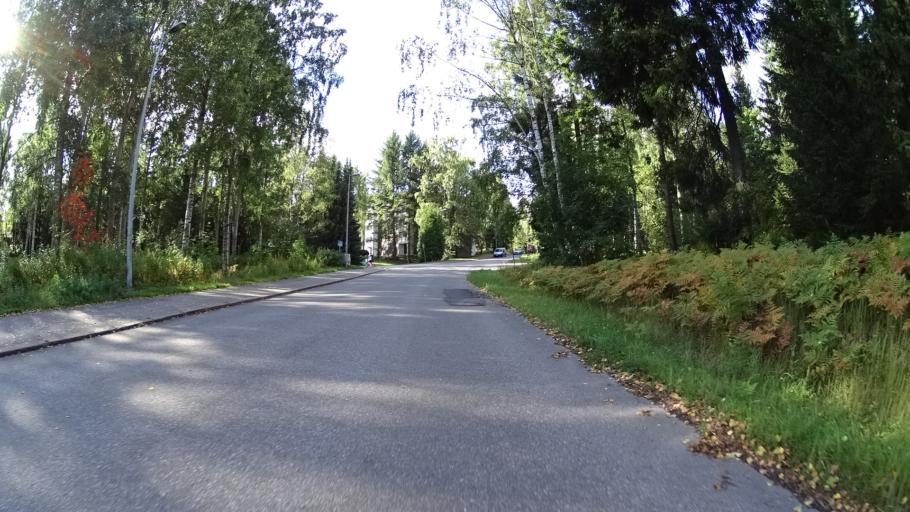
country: FI
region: Uusimaa
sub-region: Helsinki
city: Teekkarikylae
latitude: 60.1794
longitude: 24.8548
